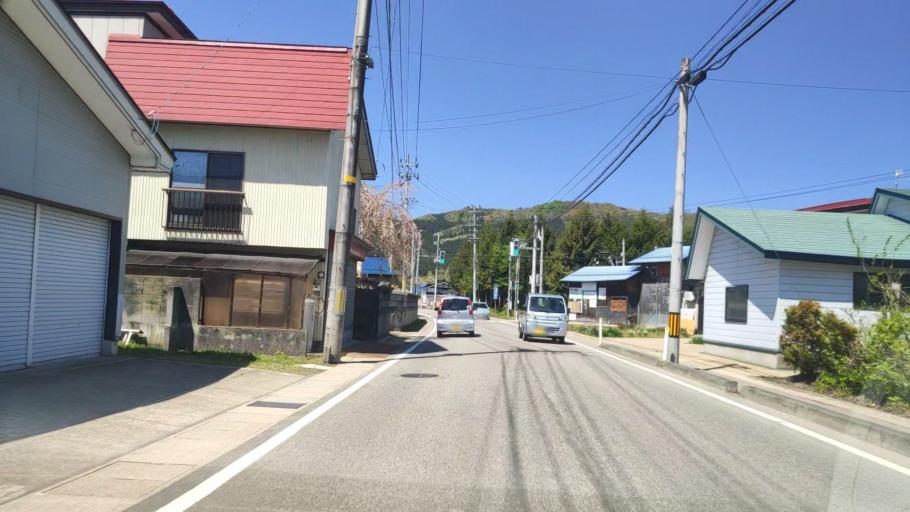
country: JP
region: Akita
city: Omagari
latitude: 39.4474
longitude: 140.4546
